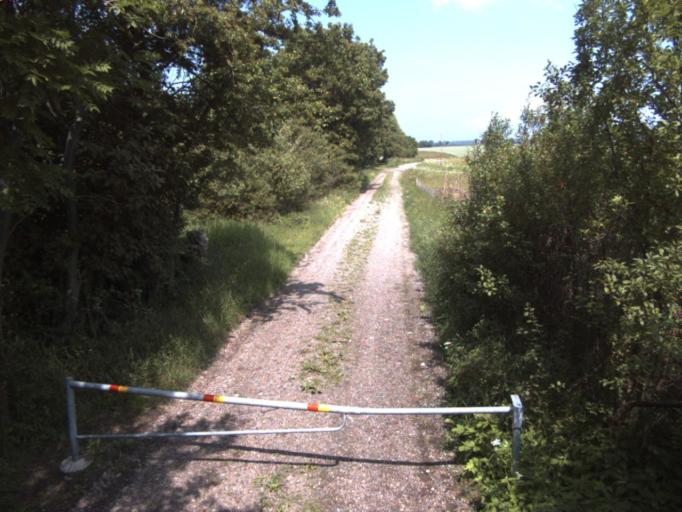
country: SE
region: Skane
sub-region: Angelholms Kommun
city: Strovelstorp
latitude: 56.1456
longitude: 12.7802
